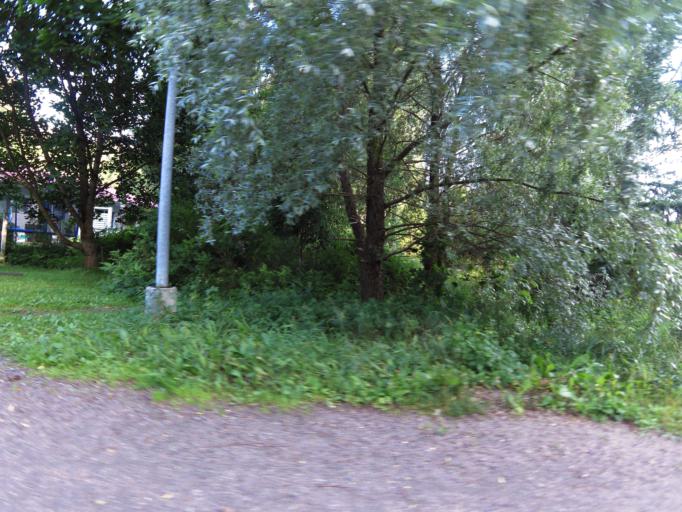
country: FI
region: Uusimaa
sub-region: Helsinki
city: Espoo
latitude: 60.1601
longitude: 24.6690
